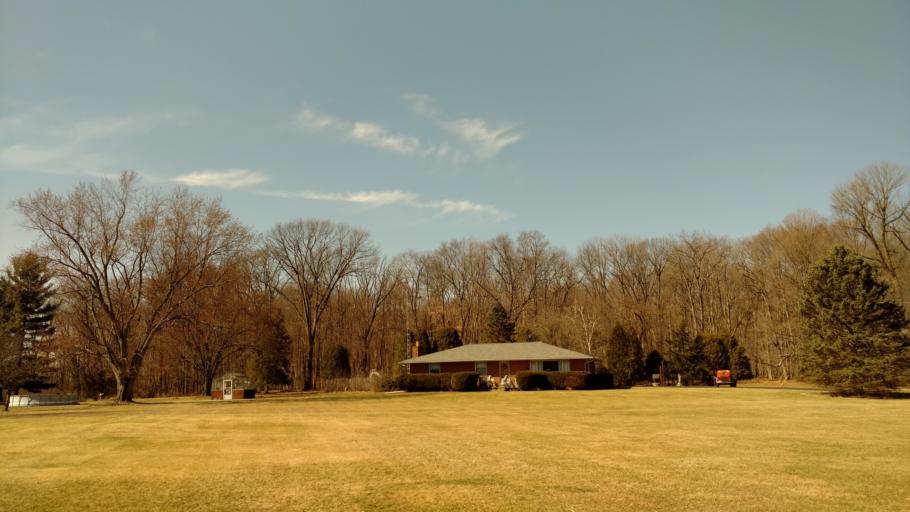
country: US
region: Ohio
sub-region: Marion County
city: Prospect
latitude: 40.5126
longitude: -83.1900
